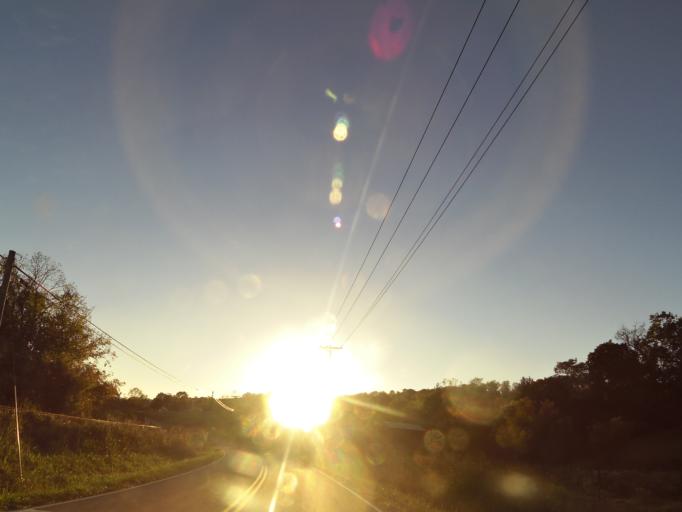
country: US
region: Tennessee
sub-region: Union County
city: Luttrell
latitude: 36.2590
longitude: -83.6622
